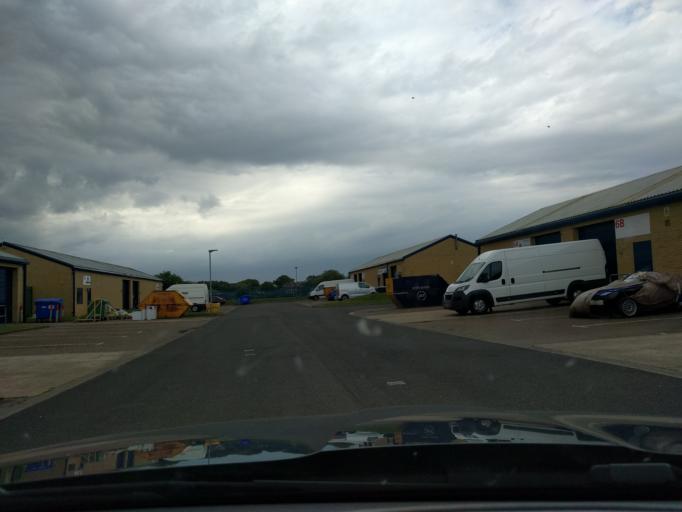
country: GB
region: England
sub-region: Northumberland
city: Amble
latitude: 55.3269
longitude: -1.5798
